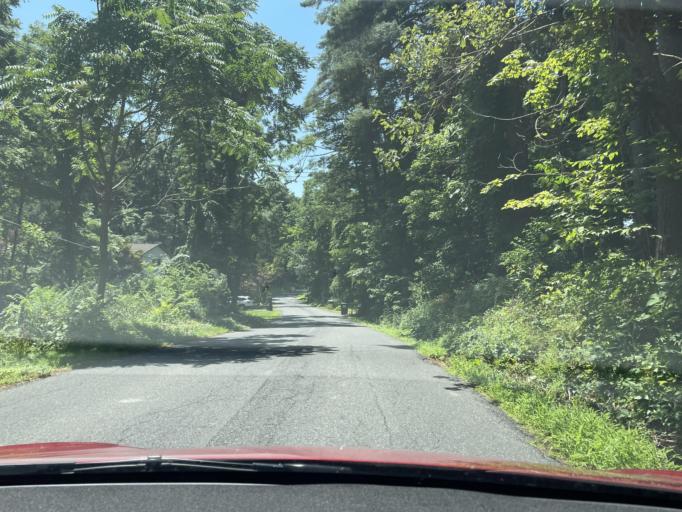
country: US
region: New York
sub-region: Ulster County
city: Glasco
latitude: 42.0280
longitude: -73.9730
